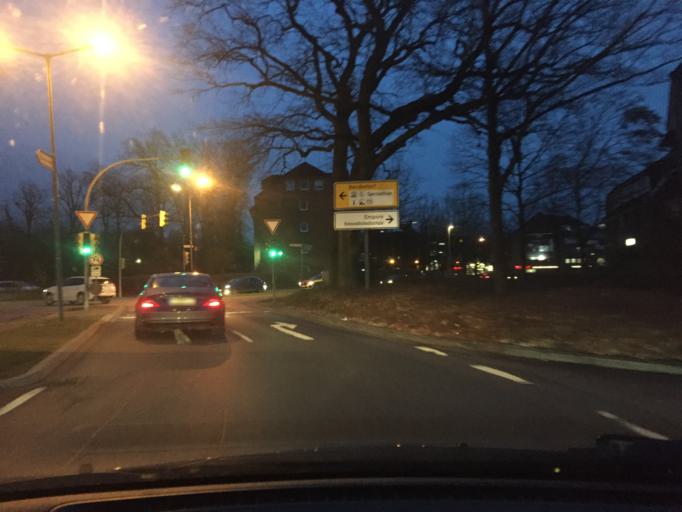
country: DE
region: Lower Saxony
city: Buchholz in der Nordheide
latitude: 53.3299
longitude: 9.8765
